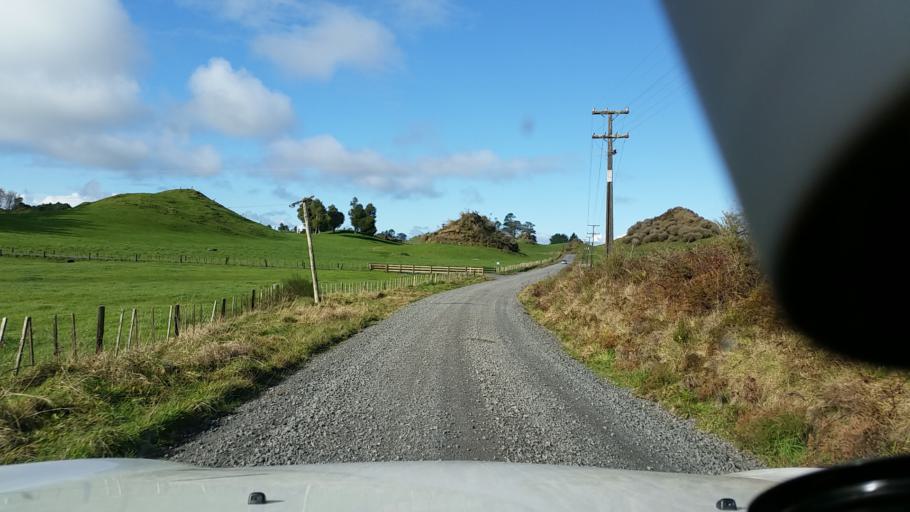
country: NZ
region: Bay of Plenty
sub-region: Rotorua District
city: Rotorua
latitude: -38.0814
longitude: 176.0499
